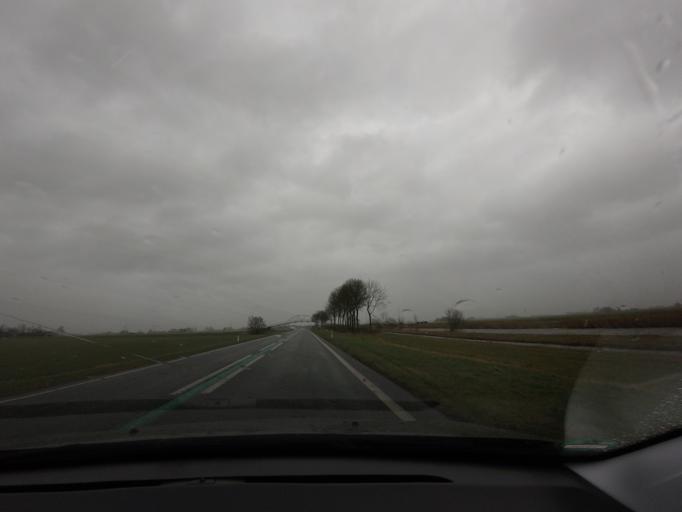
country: NL
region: Friesland
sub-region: Gemeente Littenseradiel
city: Wommels
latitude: 53.0997
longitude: 5.5642
